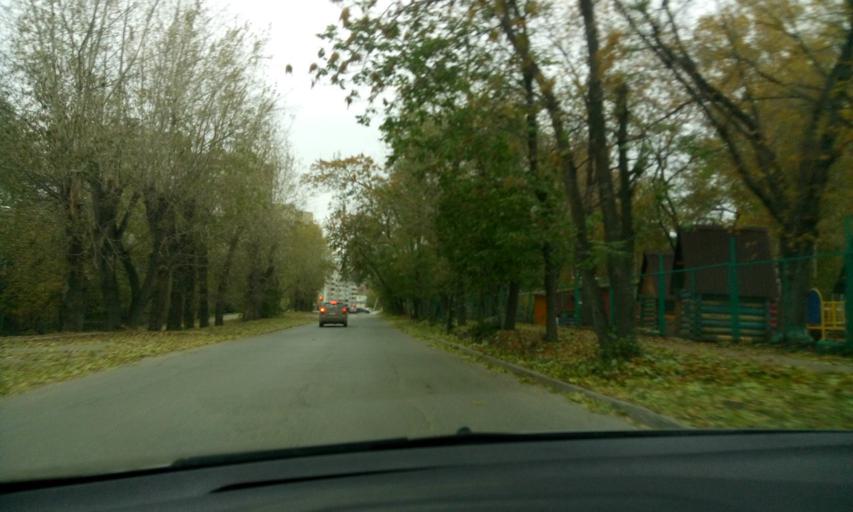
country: RU
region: Sverdlovsk
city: Yekaterinburg
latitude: 56.8610
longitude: 60.6284
